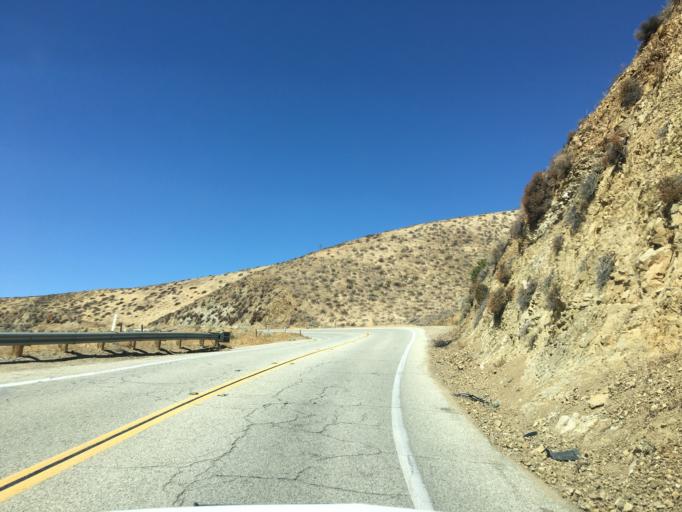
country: US
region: California
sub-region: Los Angeles County
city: Quartz Hill
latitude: 34.6103
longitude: -118.2420
